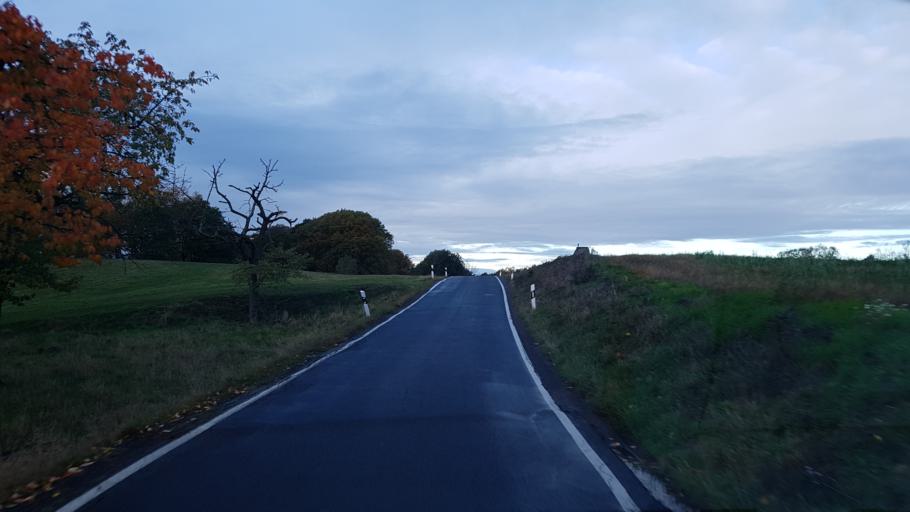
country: DE
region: Saxony
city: Dahlen
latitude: 51.3891
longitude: 13.0514
